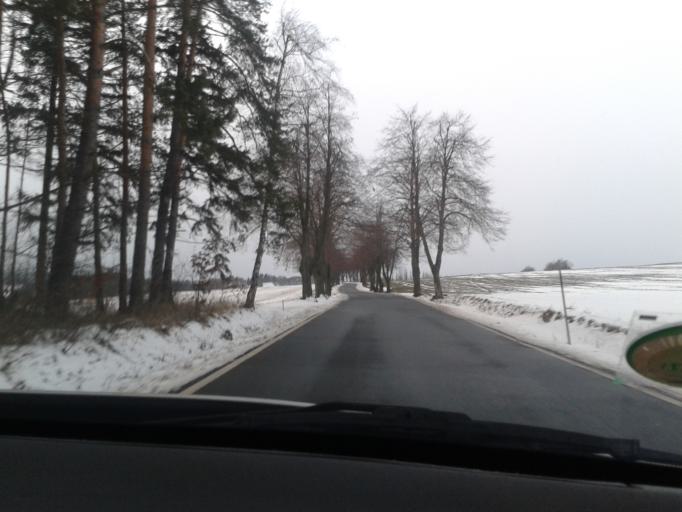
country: CZ
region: Olomoucky
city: Protivanov
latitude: 49.5261
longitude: 16.8797
